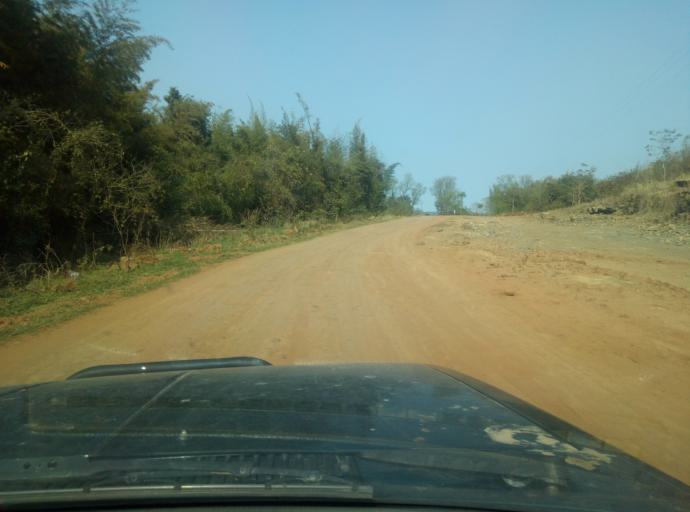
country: PY
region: Caaguazu
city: Coronel Oviedo
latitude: -25.3401
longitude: -56.3156
